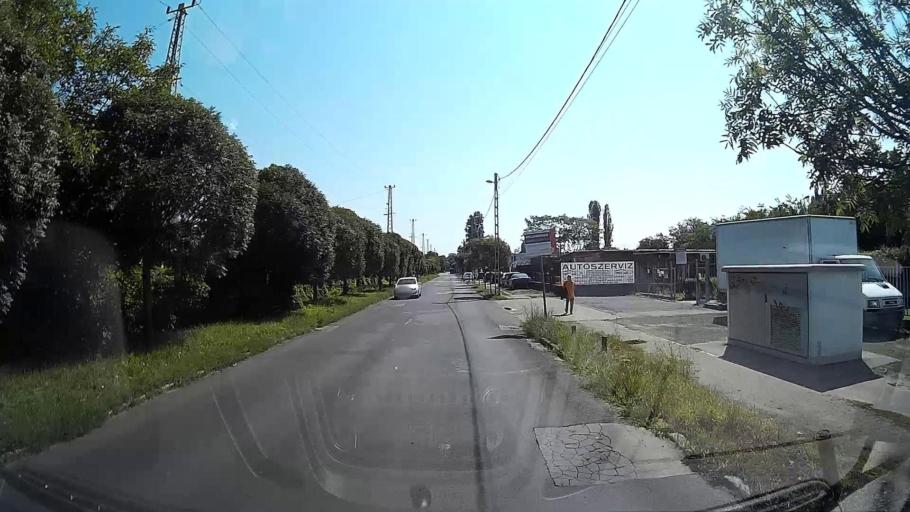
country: HU
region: Budapest
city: Budapest XVIII. keruelet
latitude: 47.4558
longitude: 19.1785
